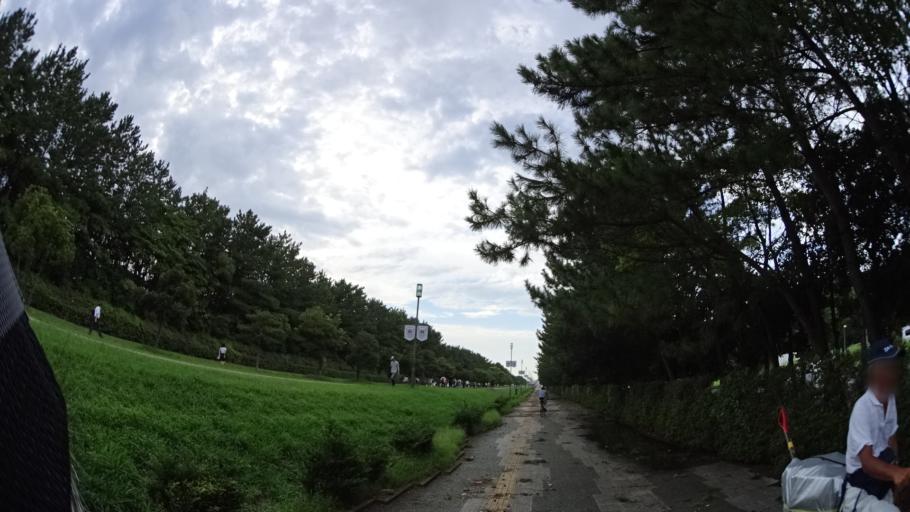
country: JP
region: Chiba
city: Funabashi
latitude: 35.6449
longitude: 140.0344
